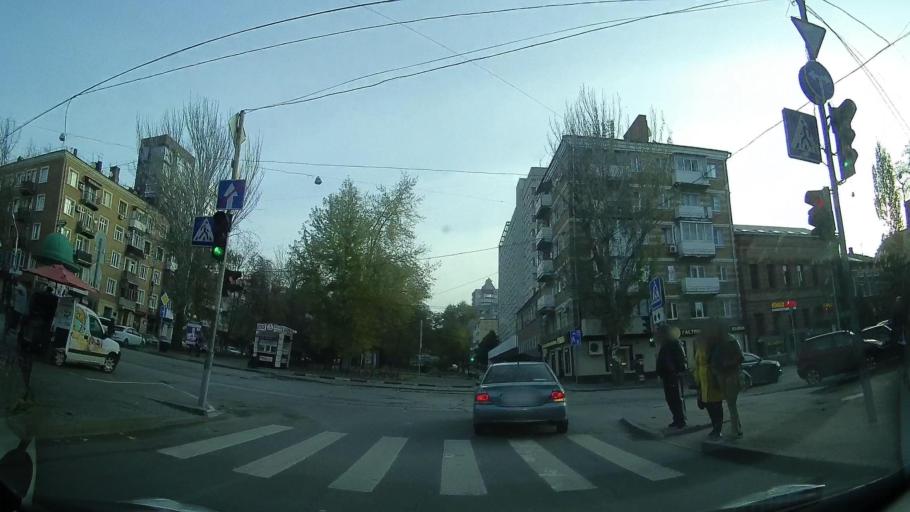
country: RU
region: Rostov
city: Rostov-na-Donu
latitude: 47.2261
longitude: 39.7199
